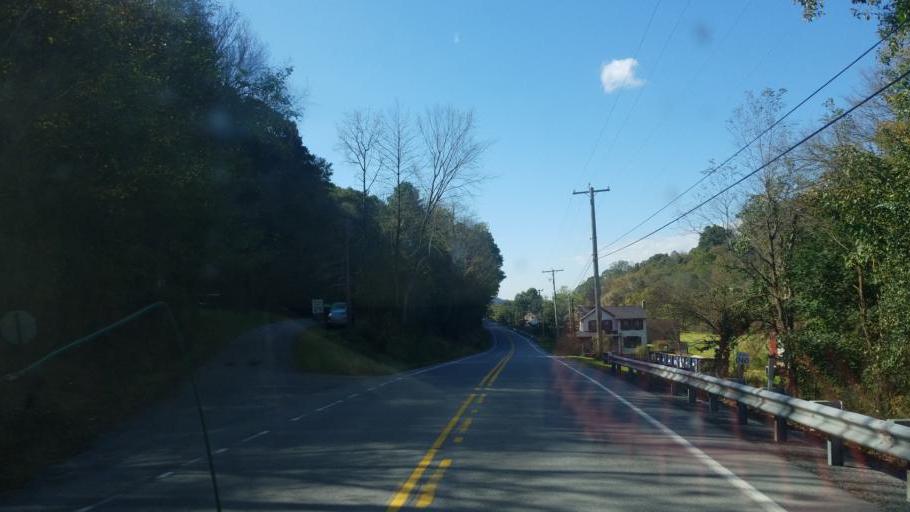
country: US
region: Pennsylvania
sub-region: Blair County
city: Claysburg
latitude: 40.1772
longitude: -78.5129
